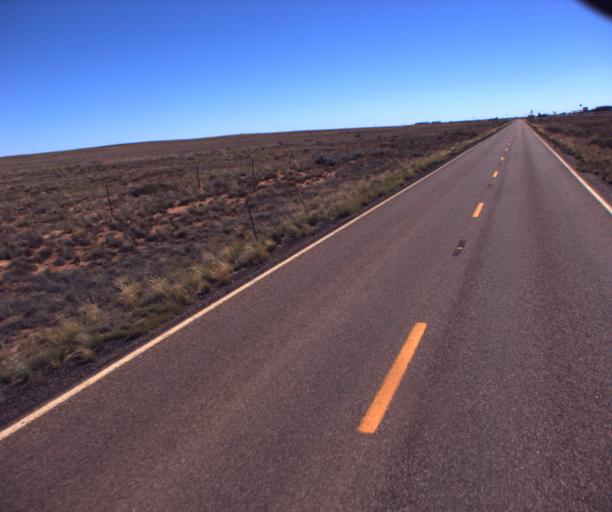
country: US
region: Arizona
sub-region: Navajo County
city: Holbrook
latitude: 34.9866
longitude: -110.0889
